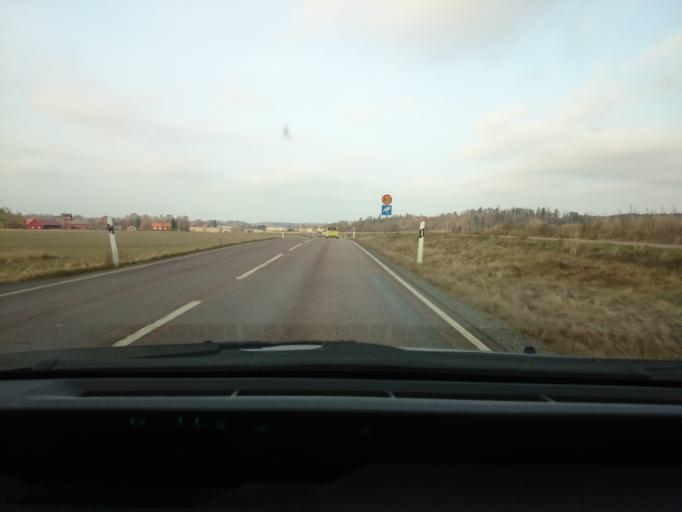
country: SE
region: Vaestmanland
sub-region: Vasteras
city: Skultuna
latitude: 59.6816
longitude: 16.4631
